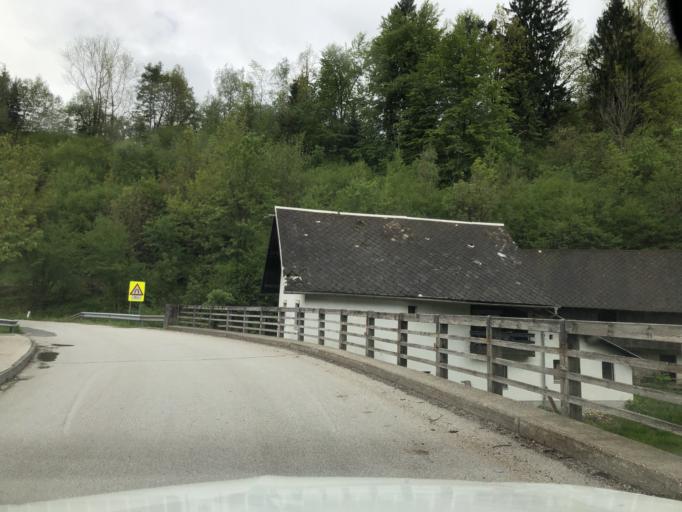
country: SI
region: Gorje
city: Zgornje Gorje
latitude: 46.3897
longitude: 14.0737
